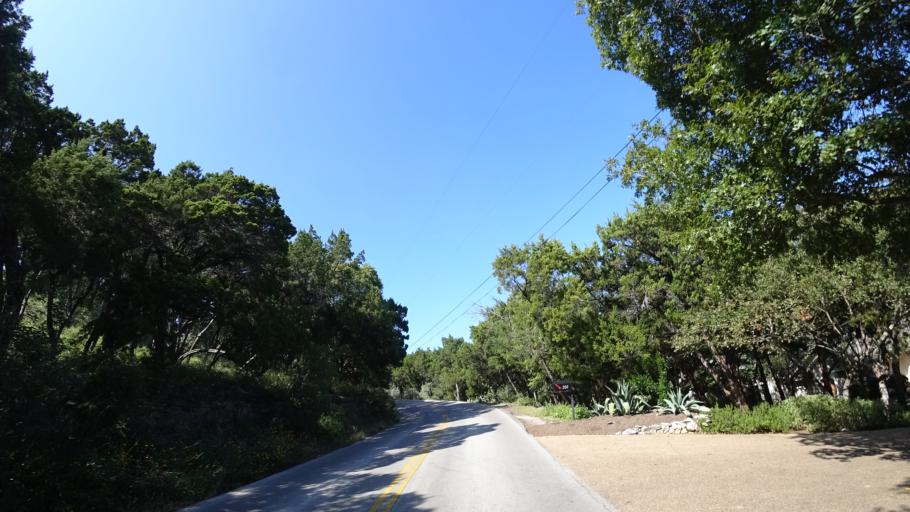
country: US
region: Texas
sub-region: Travis County
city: West Lake Hills
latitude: 30.2918
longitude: -97.8021
